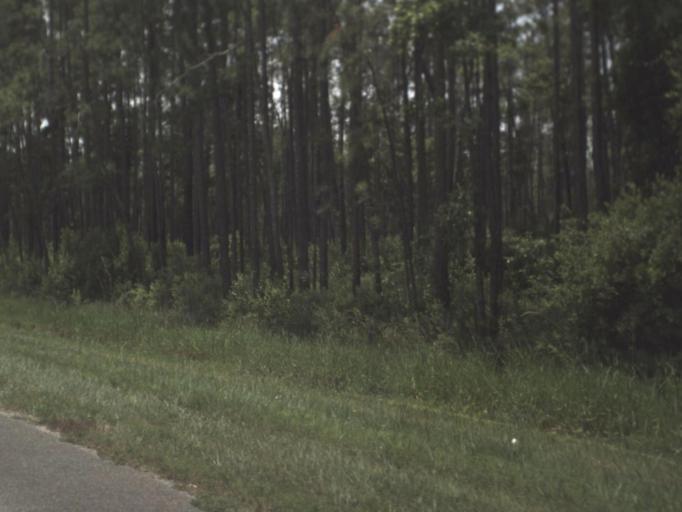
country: US
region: Florida
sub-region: Putnam County
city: Palatka
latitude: 29.4660
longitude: -81.7384
